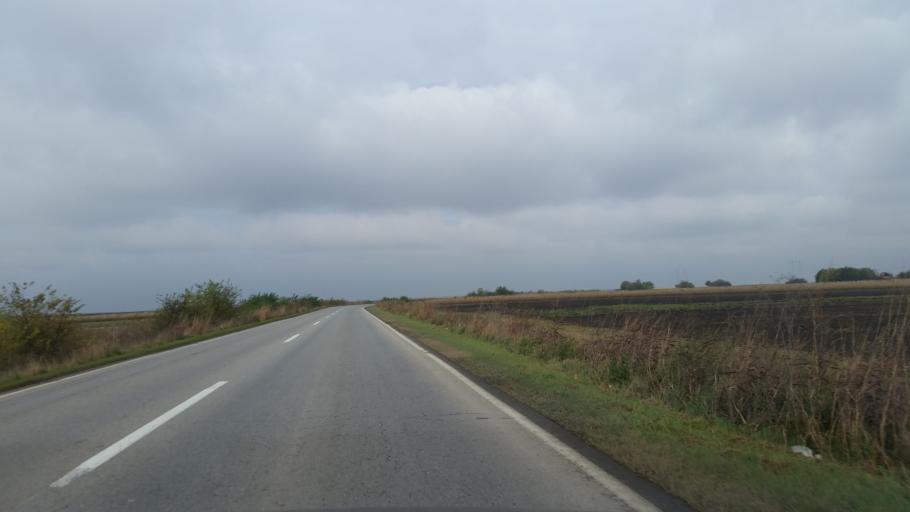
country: RS
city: Elemir
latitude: 45.4633
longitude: 20.3459
